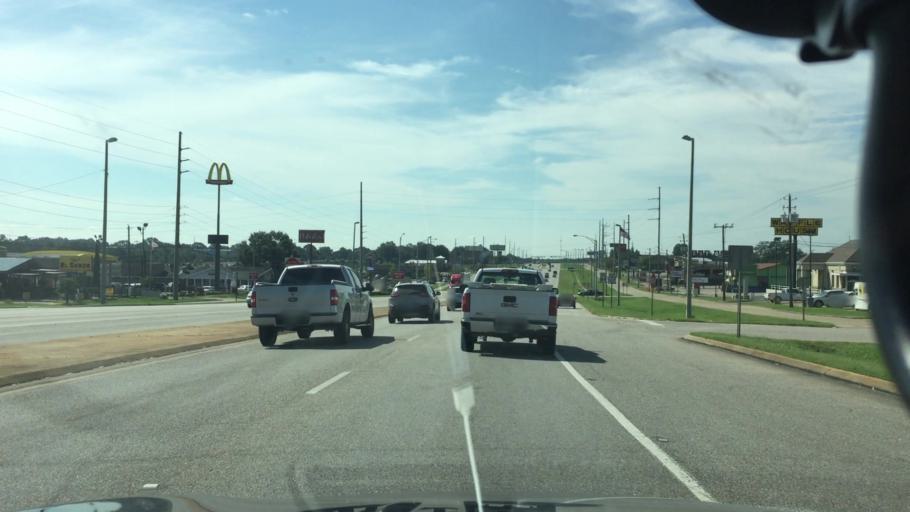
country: US
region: Alabama
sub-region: Coffee County
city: Enterprise
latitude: 31.3226
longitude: -85.8312
